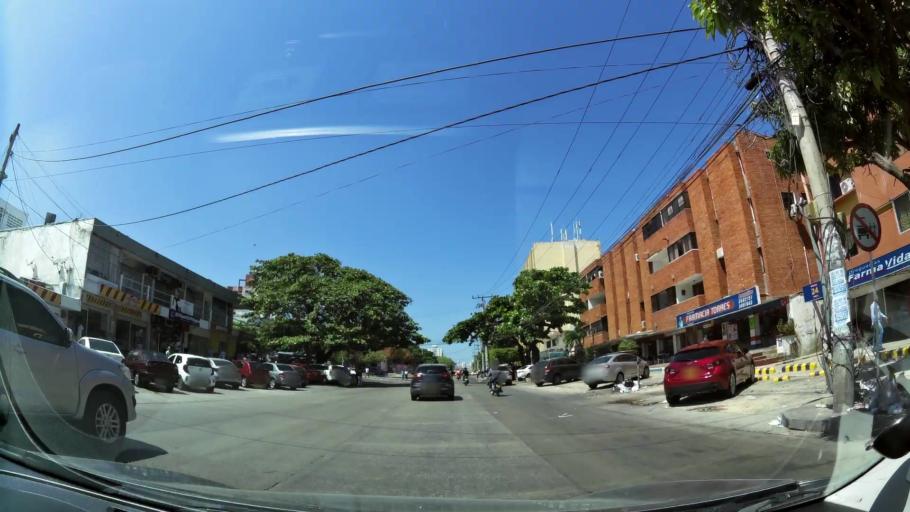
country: CO
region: Atlantico
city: Barranquilla
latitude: 10.9917
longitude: -74.8074
